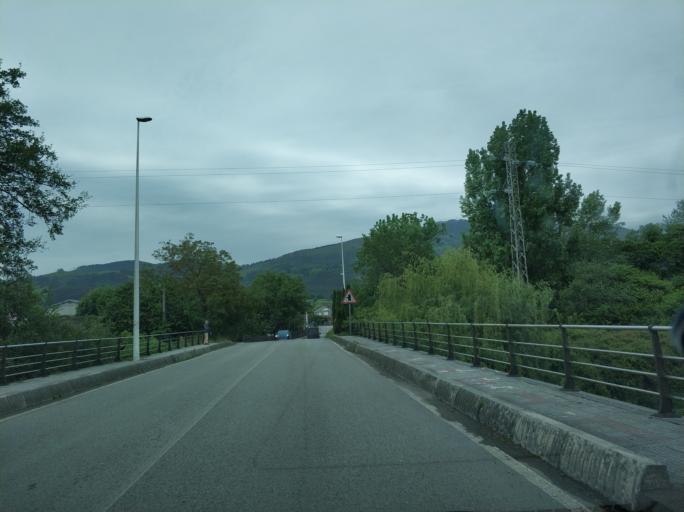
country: ES
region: Cantabria
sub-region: Provincia de Cantabria
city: Santa Maria de Cayon
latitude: 43.3150
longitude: -3.8798
